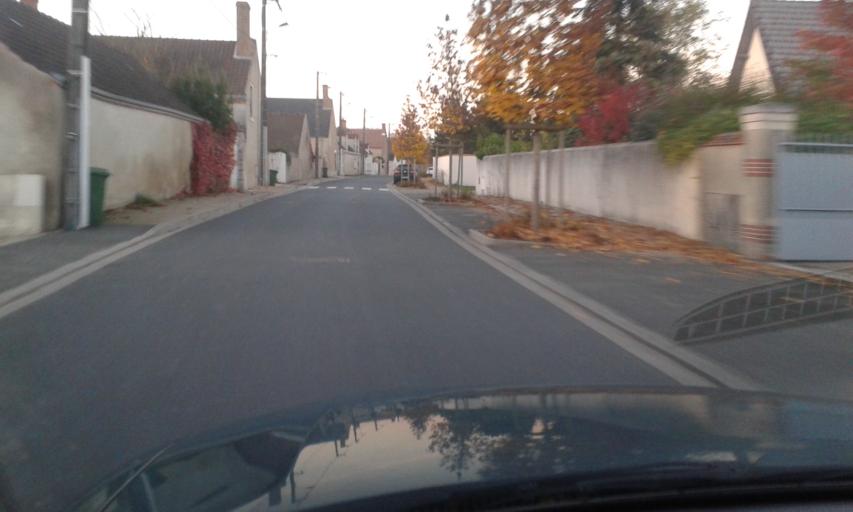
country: FR
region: Centre
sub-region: Departement du Loiret
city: Olivet
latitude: 47.8518
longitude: 1.8827
